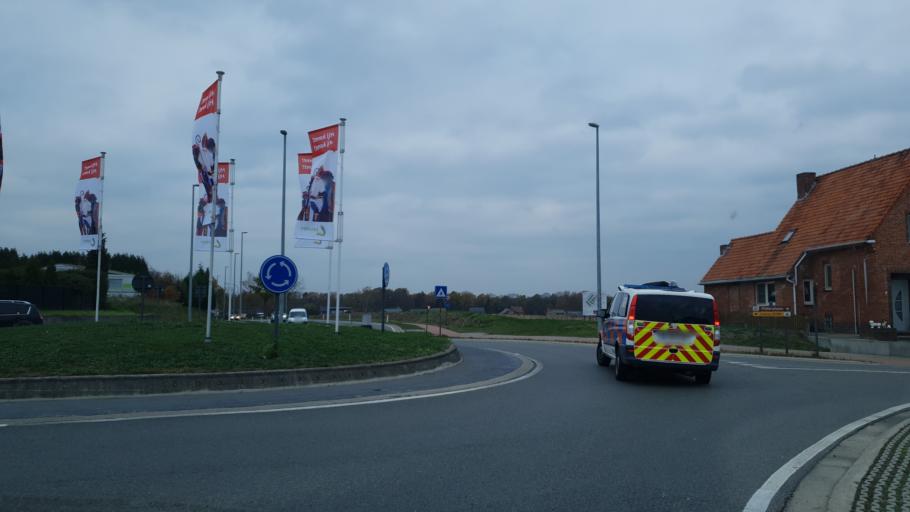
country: BE
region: Flanders
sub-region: Provincie Limburg
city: Lanaken
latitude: 50.8972
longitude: 5.6459
